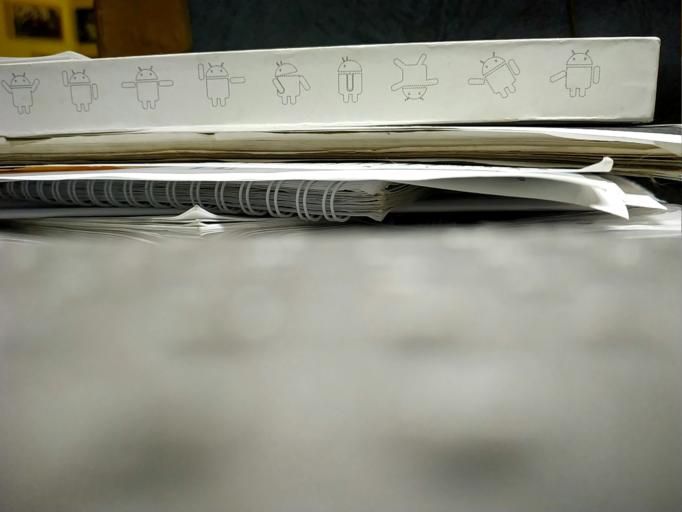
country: EE
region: Ida-Virumaa
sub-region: Narva linn
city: Narva
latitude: 59.4711
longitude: 28.2022
